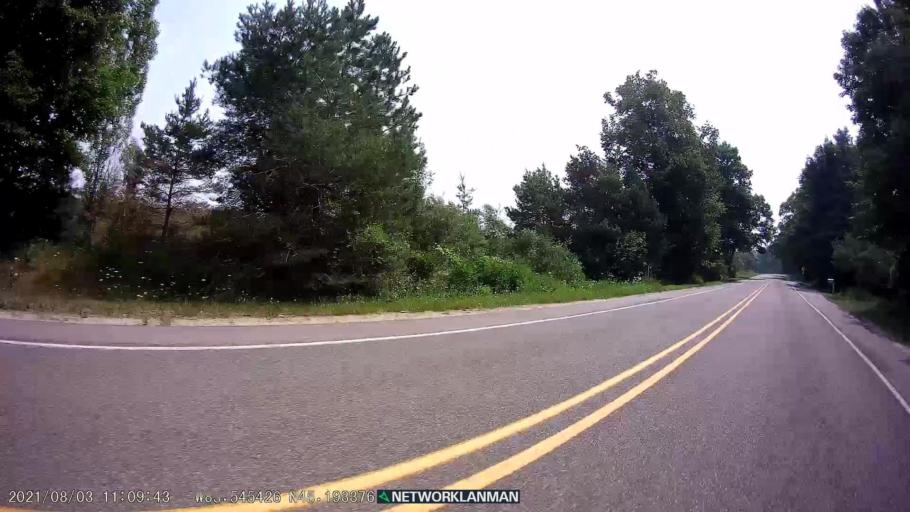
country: US
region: Michigan
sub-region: Leelanau County
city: Leland
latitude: 45.1929
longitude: -85.5454
